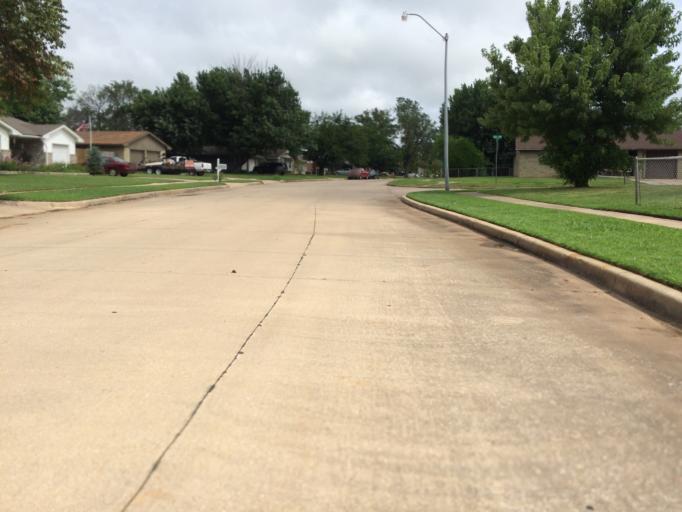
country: US
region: Oklahoma
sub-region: Cleveland County
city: Hall Park
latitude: 35.2231
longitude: -97.4182
